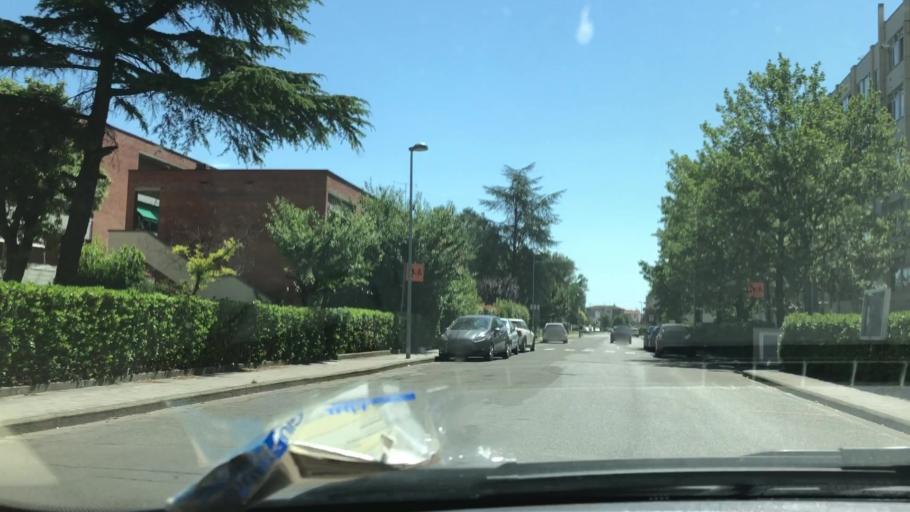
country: IT
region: Tuscany
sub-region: Province of Pisa
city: Pontedera
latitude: 43.6563
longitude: 10.6268
